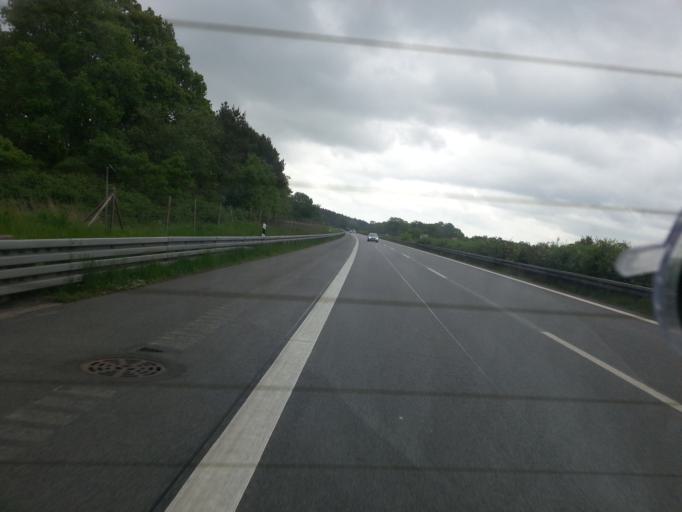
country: DE
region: Mecklenburg-Vorpommern
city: Malchow
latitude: 53.5124
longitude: 12.3634
